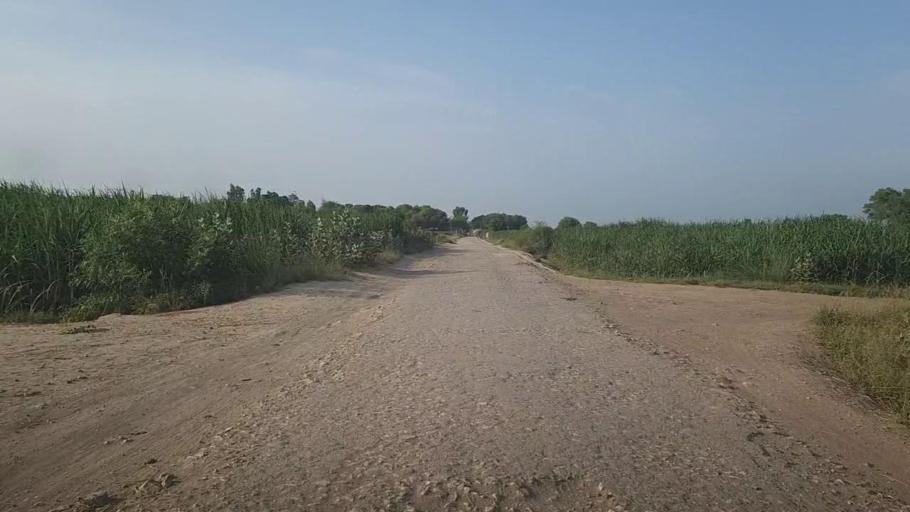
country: PK
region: Sindh
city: Ubauro
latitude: 28.3230
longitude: 69.7958
